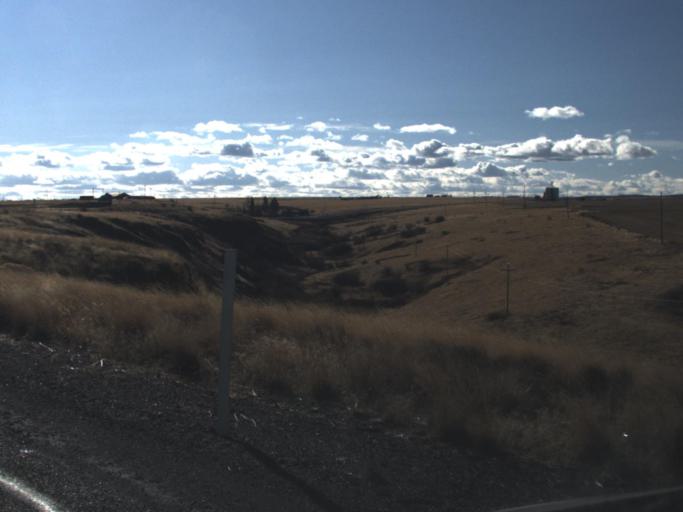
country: US
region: Washington
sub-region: Asotin County
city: Asotin
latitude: 46.2029
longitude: -117.0696
